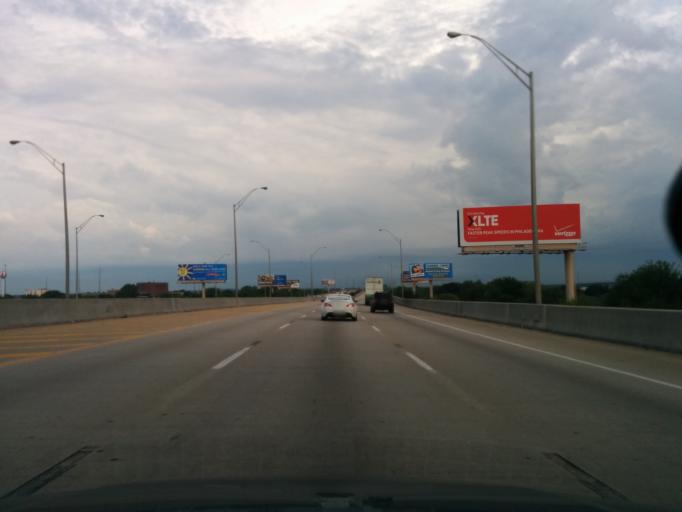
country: US
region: New Jersey
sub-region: Gloucester County
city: National Park
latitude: 39.8870
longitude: -75.2149
